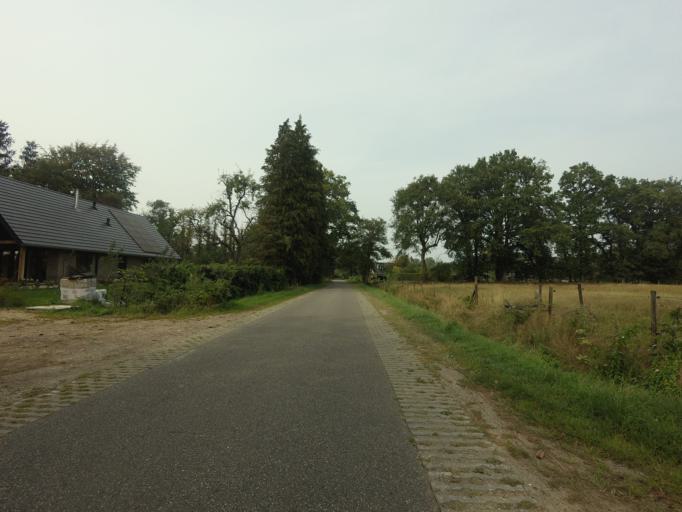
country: NL
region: Drenthe
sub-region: Gemeente Tynaarlo
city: Vries
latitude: 53.1226
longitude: 6.5684
